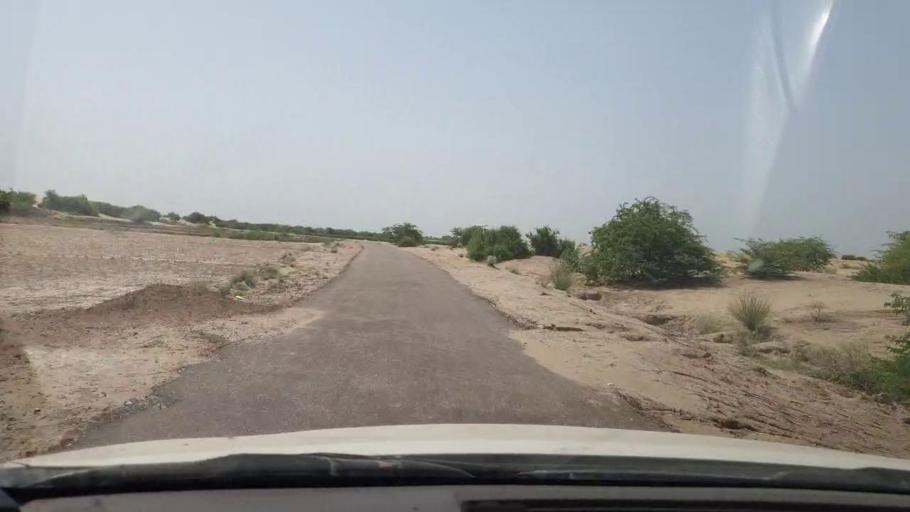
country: PK
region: Sindh
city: Rohri
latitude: 27.5200
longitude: 69.0736
